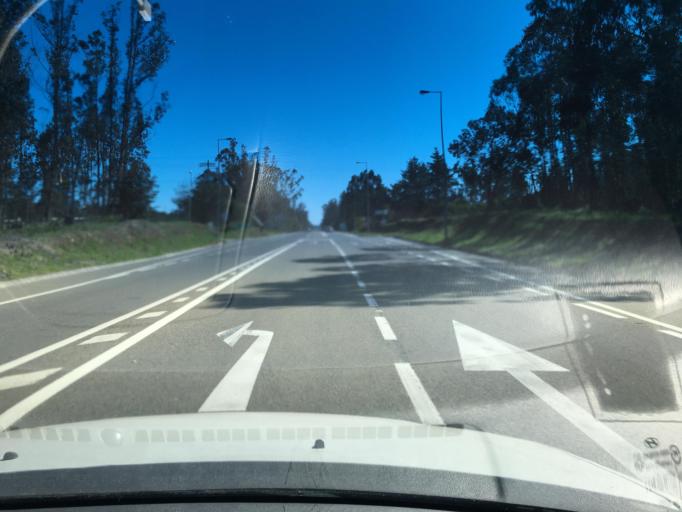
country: CL
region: Valparaiso
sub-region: San Antonio Province
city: El Tabo
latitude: -33.3998
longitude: -71.5879
